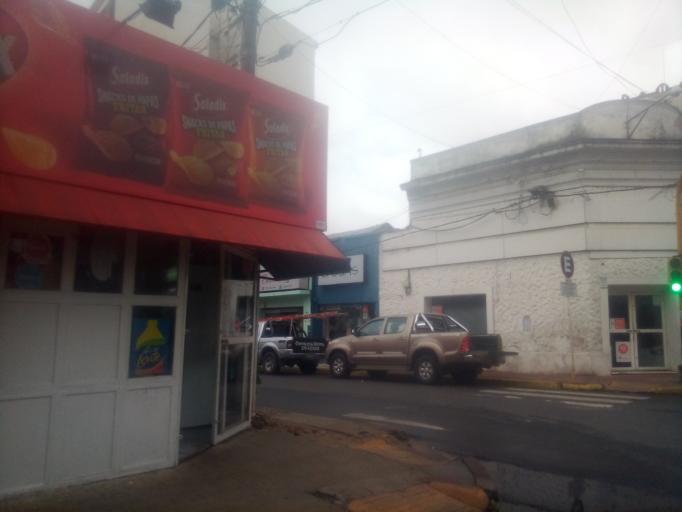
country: AR
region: Corrientes
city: Corrientes
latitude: -27.4666
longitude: -58.8356
